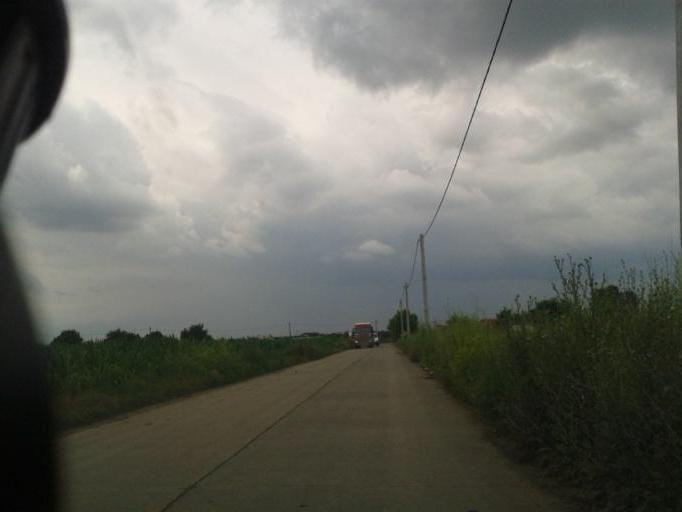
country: RO
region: Calarasi
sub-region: Comuna Fundulea
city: Fundulea
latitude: 44.4948
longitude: 26.5013
